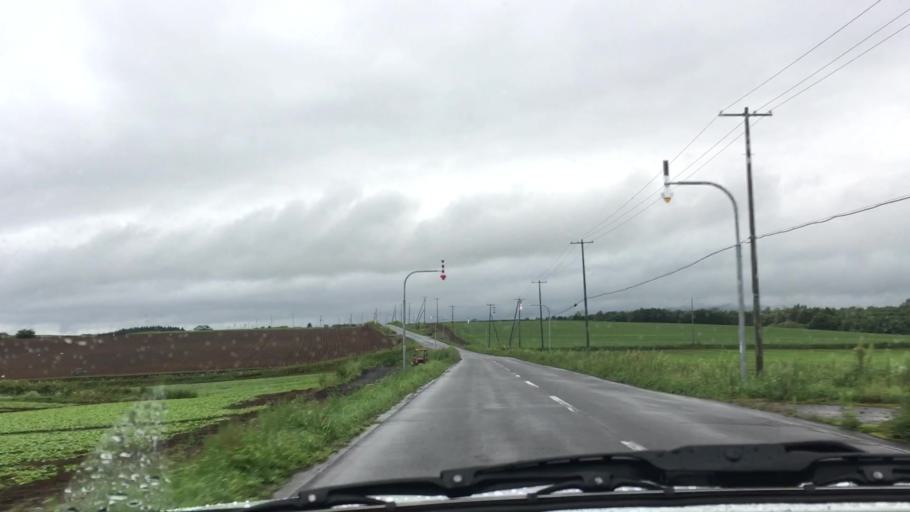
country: JP
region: Hokkaido
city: Niseko Town
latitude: 42.6817
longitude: 140.8054
